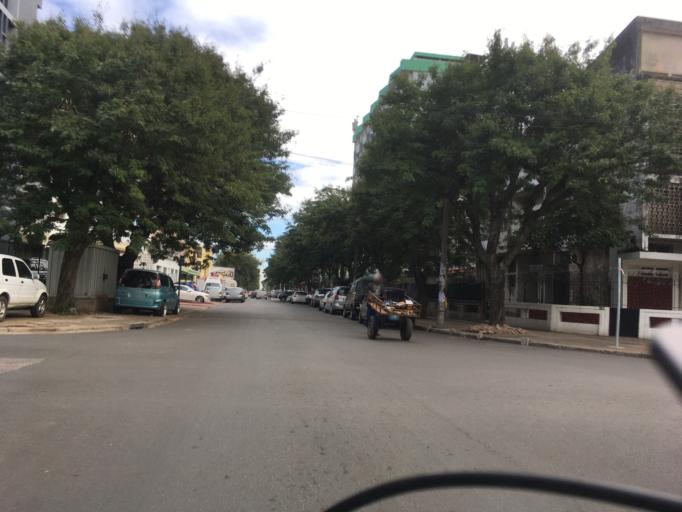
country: MZ
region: Maputo City
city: Maputo
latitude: -25.9642
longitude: 32.5873
